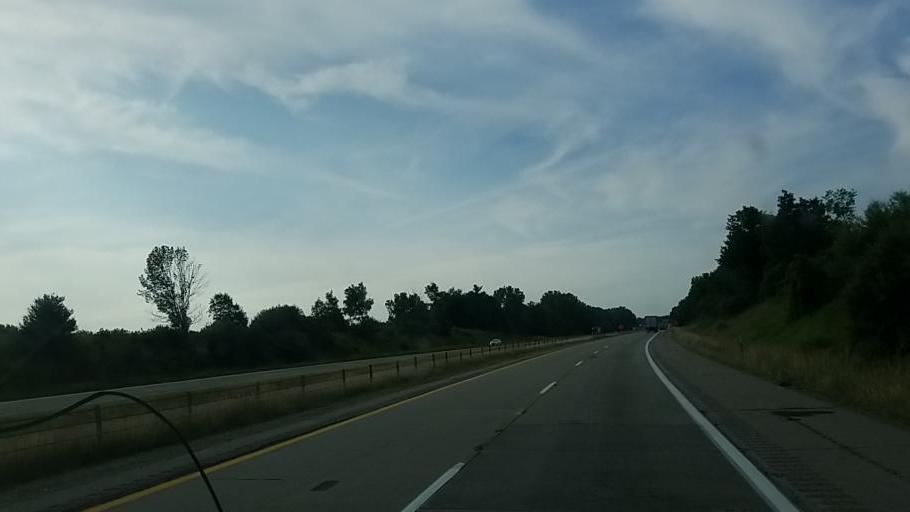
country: US
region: Michigan
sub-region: Ionia County
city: Portland
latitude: 42.8416
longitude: -84.8481
